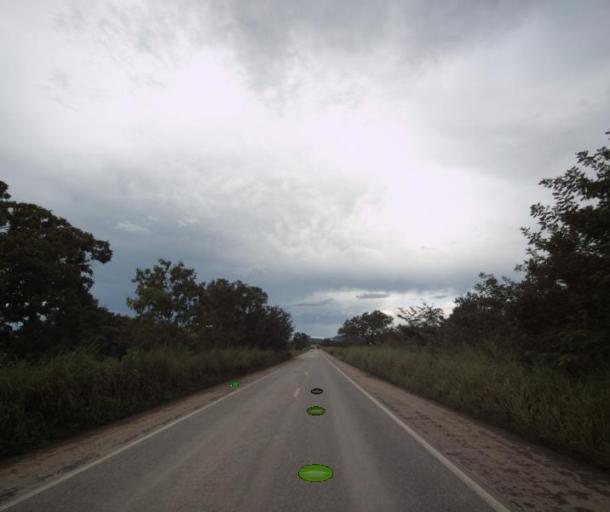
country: BR
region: Goias
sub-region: Porangatu
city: Porangatu
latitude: -13.5666
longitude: -49.0521
